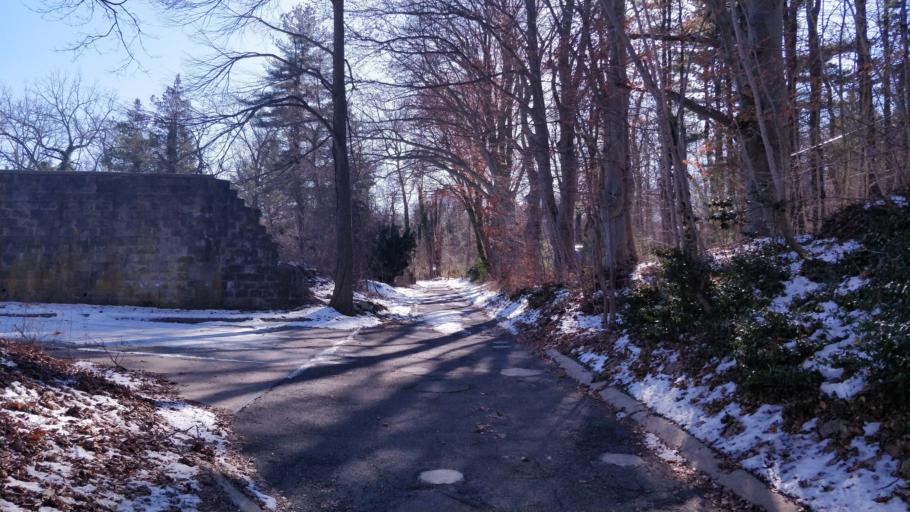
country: US
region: New York
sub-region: Nassau County
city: Brookville
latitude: 40.8088
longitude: -73.5841
